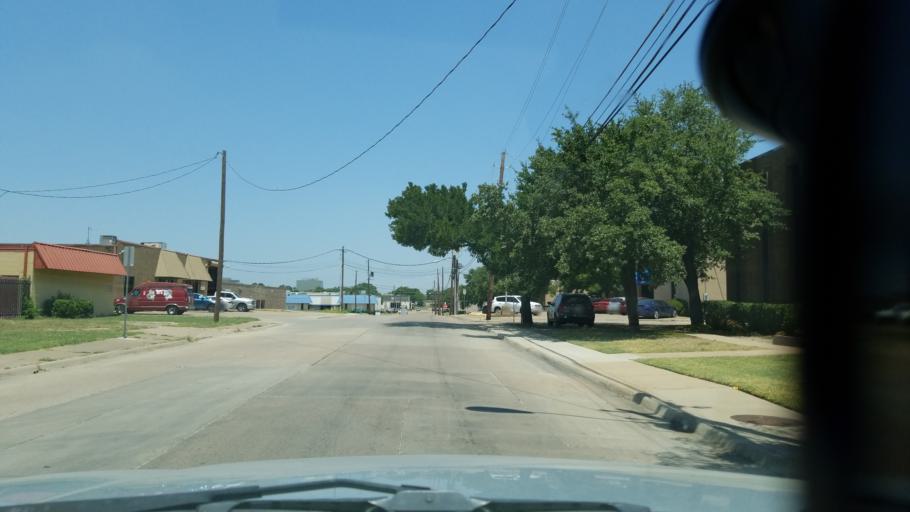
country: US
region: Texas
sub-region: Dallas County
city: Farmers Branch
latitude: 32.8986
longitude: -96.8836
